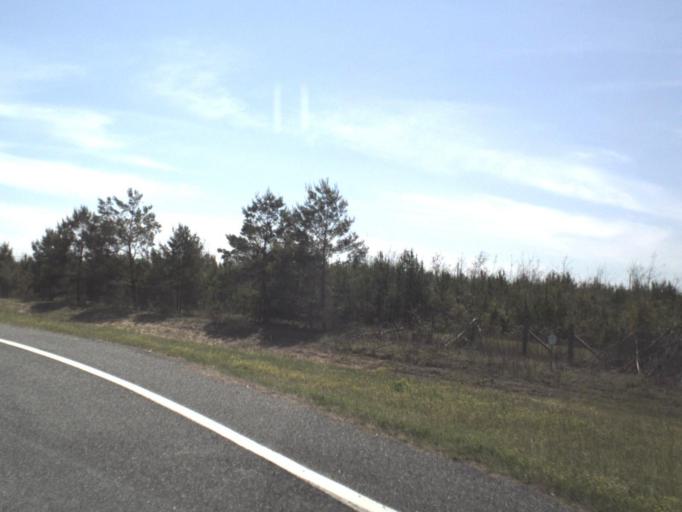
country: US
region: Florida
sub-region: Bay County
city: Lynn Haven
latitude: 30.4154
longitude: -85.6908
